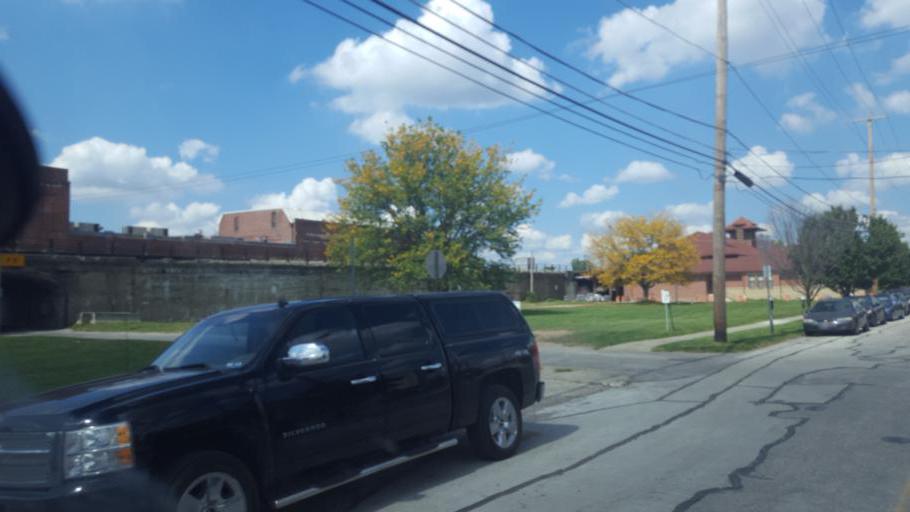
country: US
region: Ohio
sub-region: Franklin County
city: Columbus
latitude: 39.9595
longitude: -83.0100
